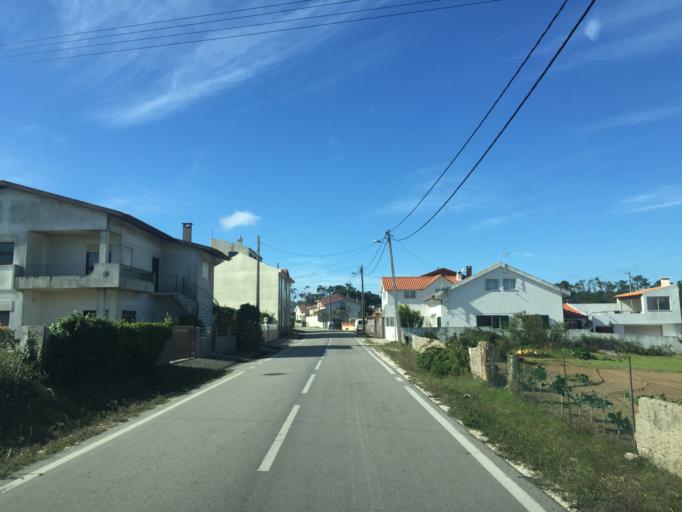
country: PT
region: Coimbra
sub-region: Figueira da Foz
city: Buarcos
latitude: 40.1911
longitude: -8.8659
